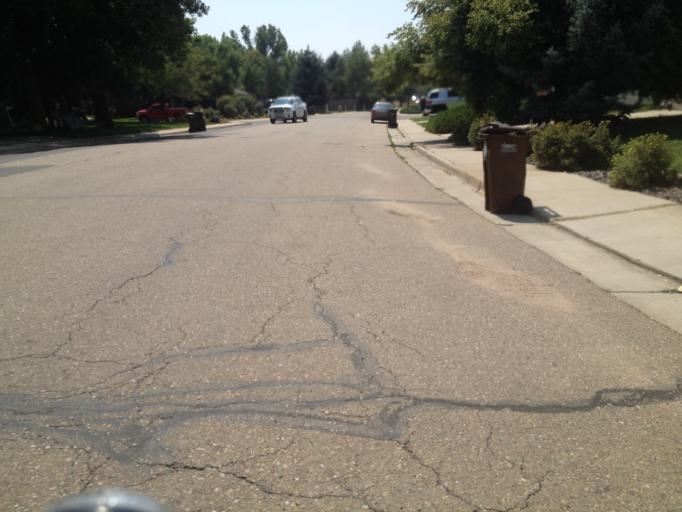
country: US
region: Colorado
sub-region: Boulder County
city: Louisville
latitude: 39.9715
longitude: -105.1380
